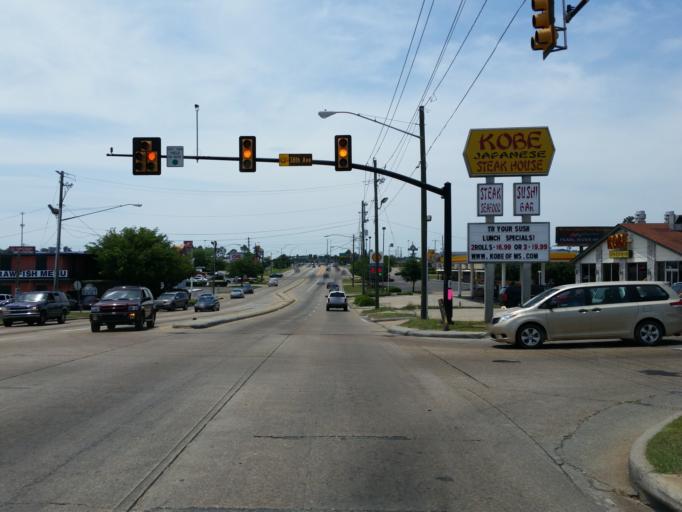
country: US
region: Mississippi
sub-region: Lamar County
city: Arnold Line
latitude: 31.3251
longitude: -89.3454
